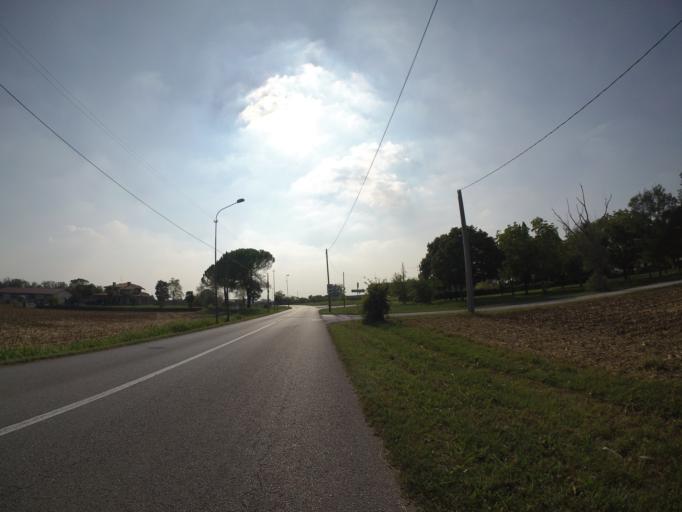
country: IT
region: Friuli Venezia Giulia
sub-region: Provincia di Udine
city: Sedegliano
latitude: 45.9951
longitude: 13.0220
